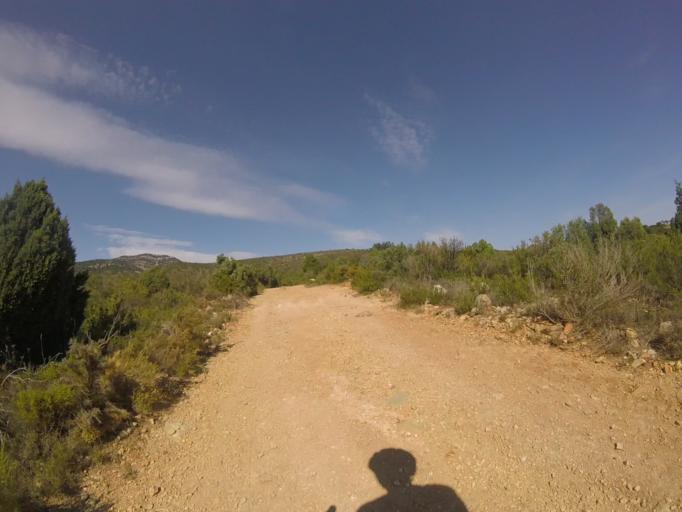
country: ES
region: Valencia
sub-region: Provincia de Castello
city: Sierra-Engarceran
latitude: 40.2711
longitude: 0.0154
